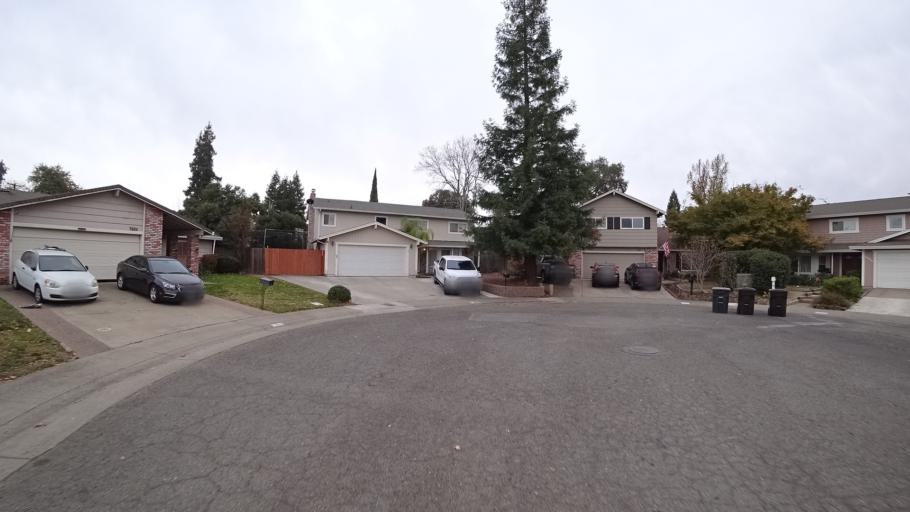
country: US
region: California
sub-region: Sacramento County
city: Citrus Heights
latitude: 38.7006
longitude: -121.3024
